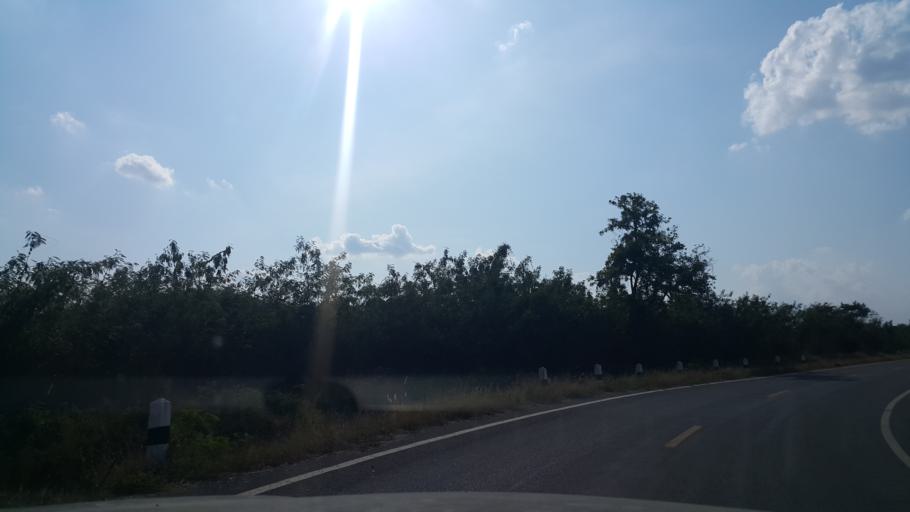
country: TH
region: Lamphun
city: Mae Tha
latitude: 18.5223
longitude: 99.0986
